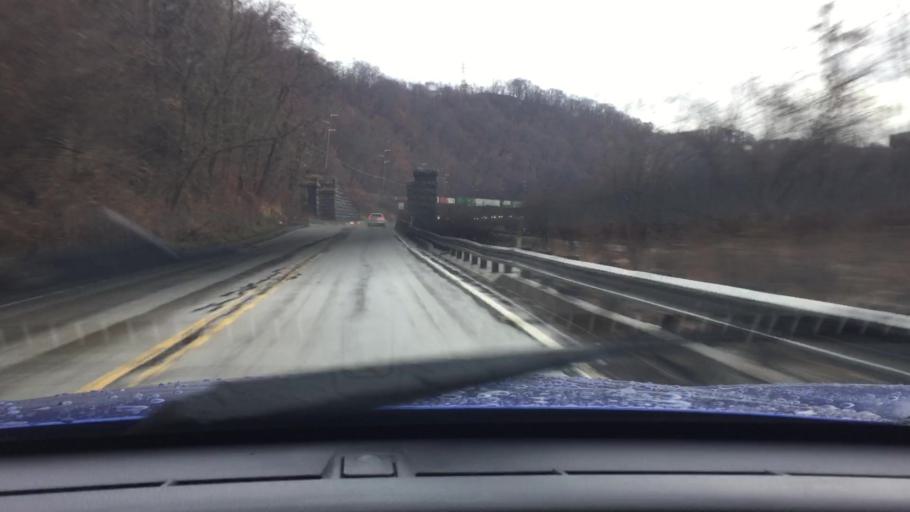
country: US
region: Pennsylvania
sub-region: Allegheny County
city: West Homestead
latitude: 40.3945
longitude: -79.9387
